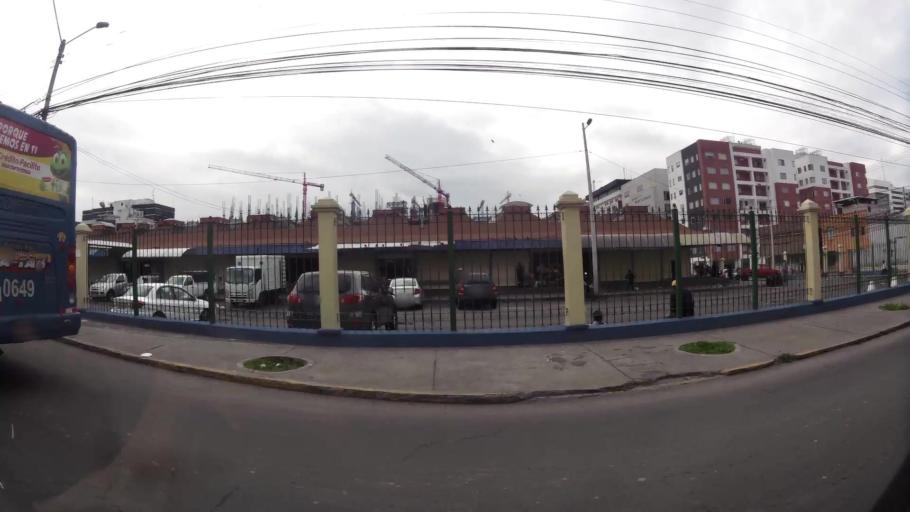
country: EC
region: Pichincha
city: Quito
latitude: -0.1722
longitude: -78.4869
